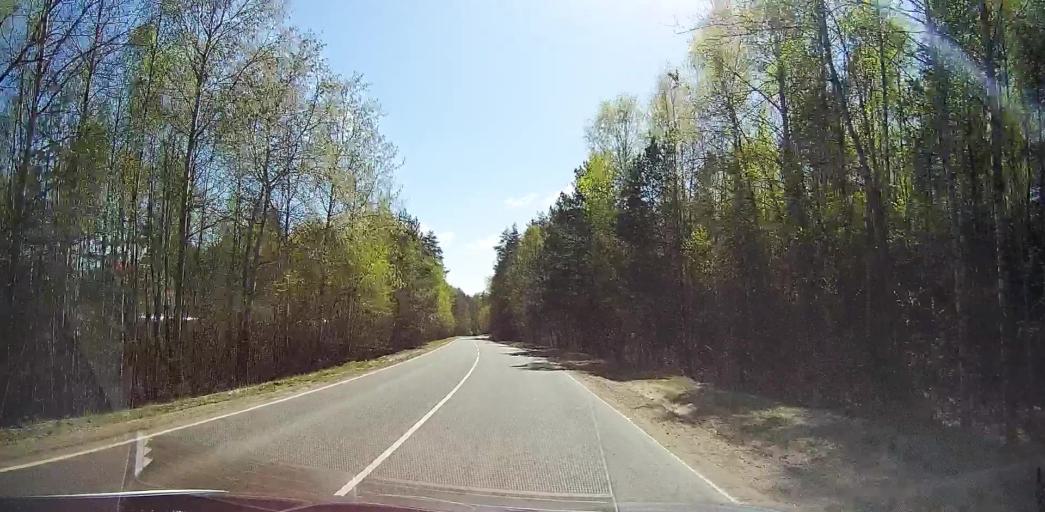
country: RU
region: Moskovskaya
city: Beloozerskiy
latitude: 55.4905
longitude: 38.4270
